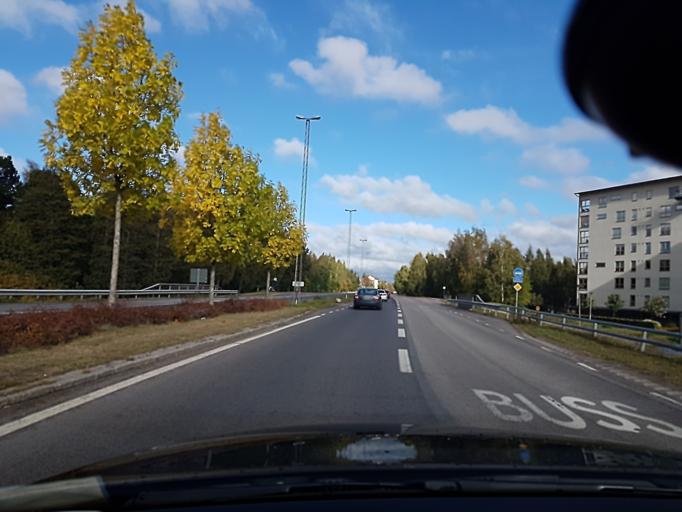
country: SE
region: Kronoberg
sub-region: Vaxjo Kommun
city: Vaexjoe
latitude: 56.8612
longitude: 14.8205
